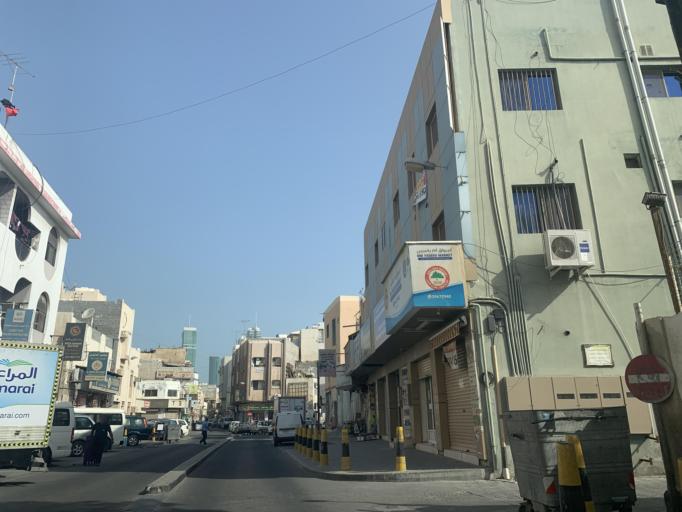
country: BH
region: Manama
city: Manama
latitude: 26.2260
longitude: 50.5770
